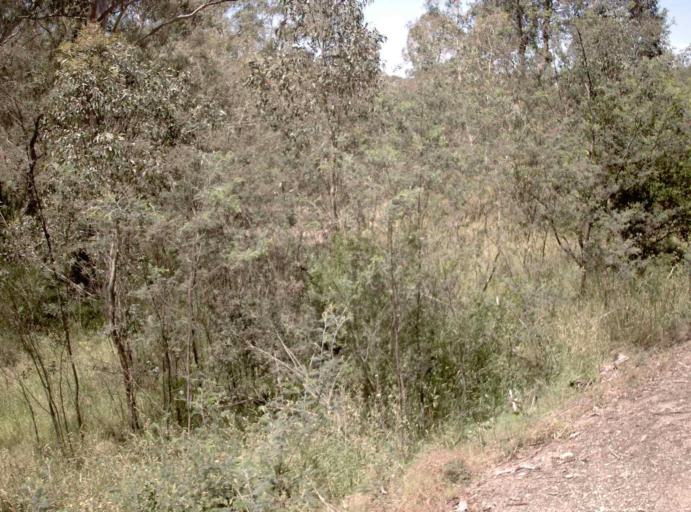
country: AU
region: Victoria
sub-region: East Gippsland
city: Bairnsdale
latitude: -37.4015
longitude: 147.8356
